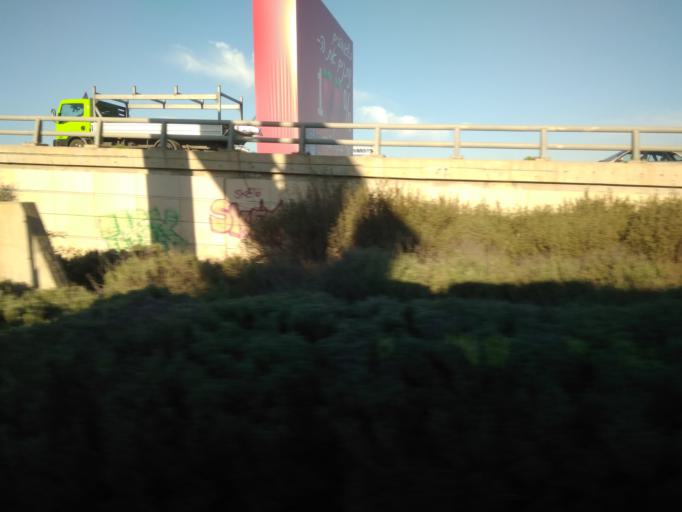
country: IL
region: Tel Aviv
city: Herzliya Pituah
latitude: 32.1429
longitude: 34.8019
